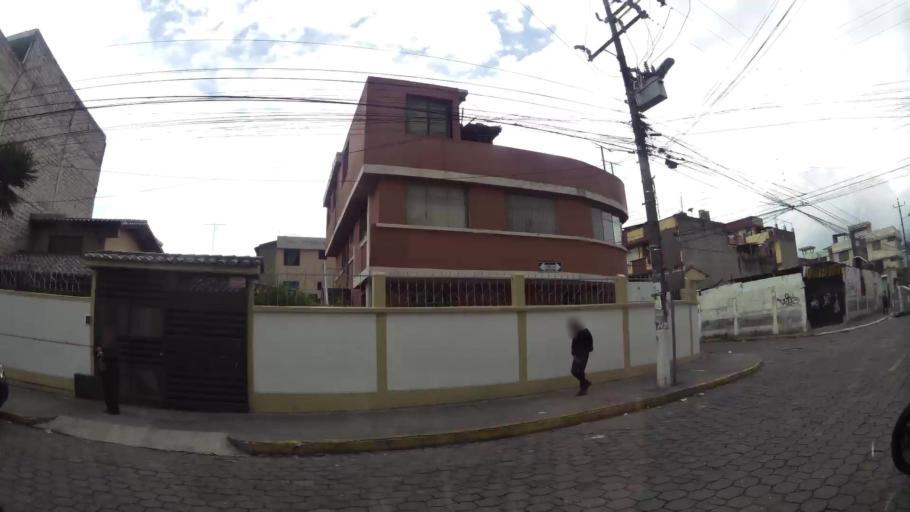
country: EC
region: Pichincha
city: Quito
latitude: -0.2830
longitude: -78.5369
